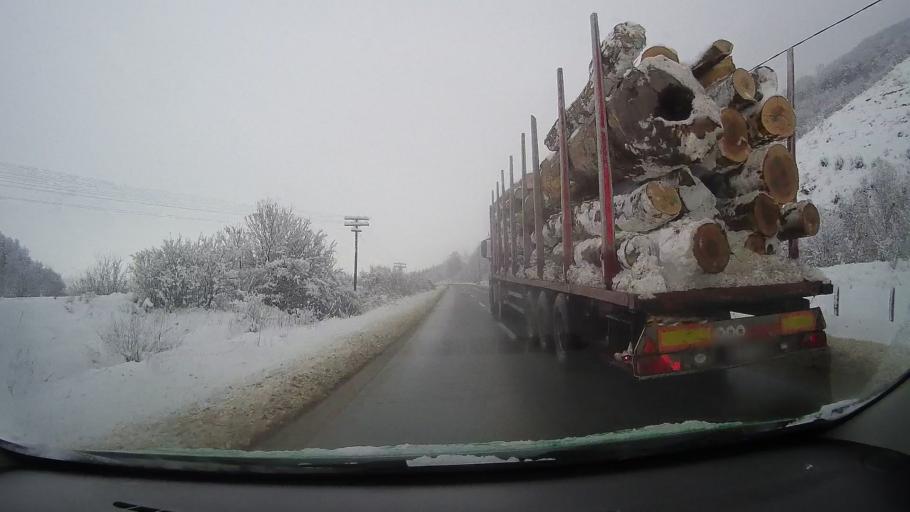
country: RO
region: Sibiu
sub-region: Comuna Orlat
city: Orlat
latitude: 45.7587
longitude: 23.9421
